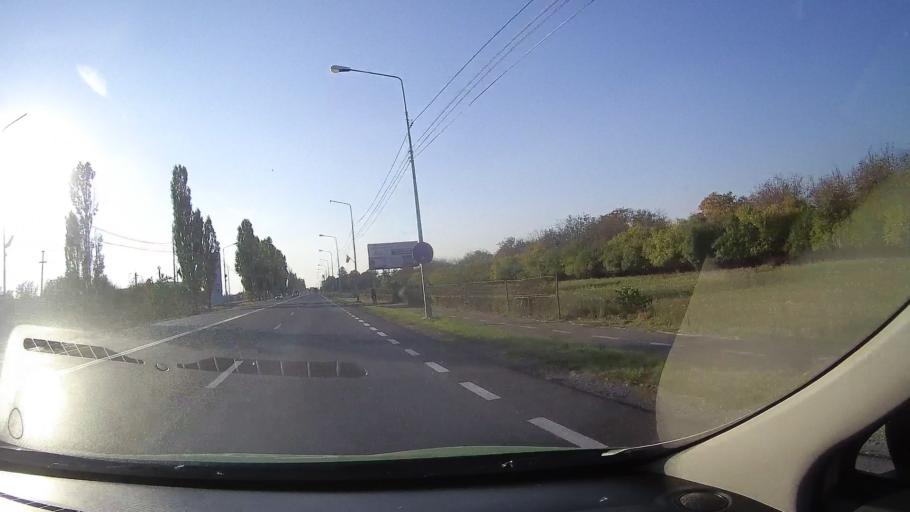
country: RO
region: Bihor
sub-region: Comuna Bors
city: Santion
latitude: 47.0997
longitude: 21.8543
